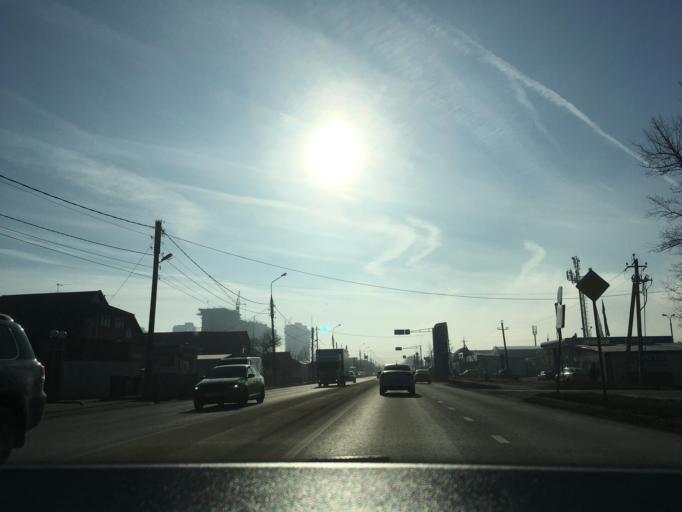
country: RU
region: Krasnodarskiy
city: Krasnodar
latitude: 45.1121
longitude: 39.0122
